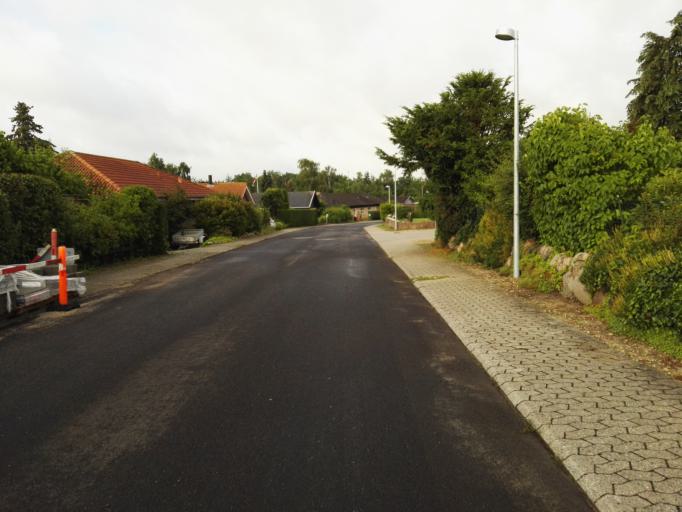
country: DK
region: Capital Region
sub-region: Ballerup Kommune
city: Ballerup
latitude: 55.7160
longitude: 12.3529
